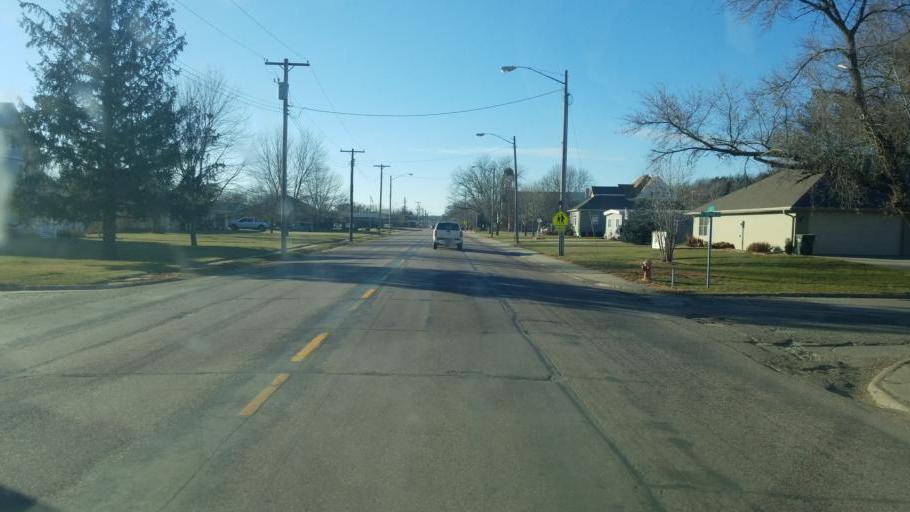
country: US
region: South Dakota
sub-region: Union County
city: Dakota Dunes
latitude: 42.4484
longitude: -96.5618
